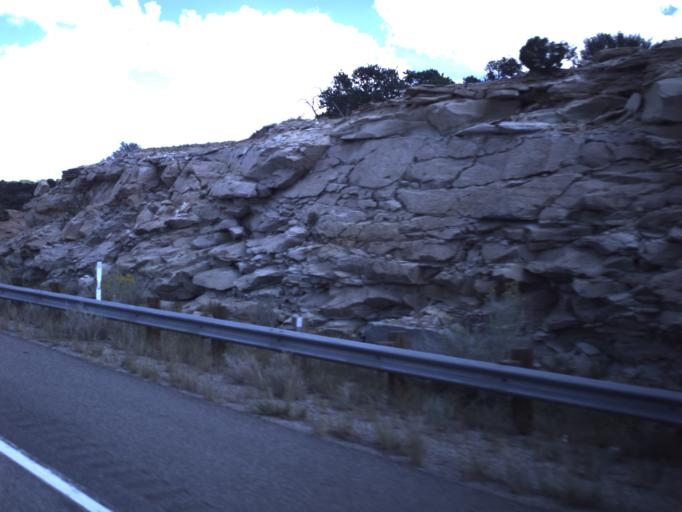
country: US
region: Utah
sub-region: Emery County
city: Ferron
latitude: 38.8589
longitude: -110.8662
